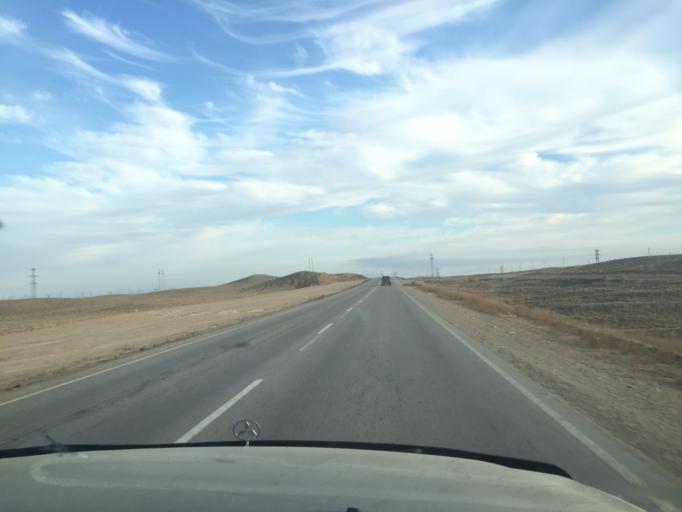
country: KZ
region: Almaty Oblysy
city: Ulken
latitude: 45.1993
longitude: 73.8972
